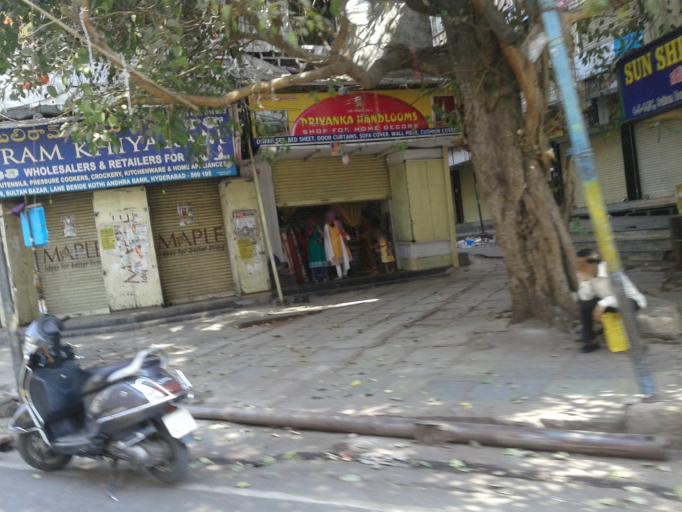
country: IN
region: Telangana
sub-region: Hyderabad
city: Hyderabad
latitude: 17.3858
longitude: 78.4851
